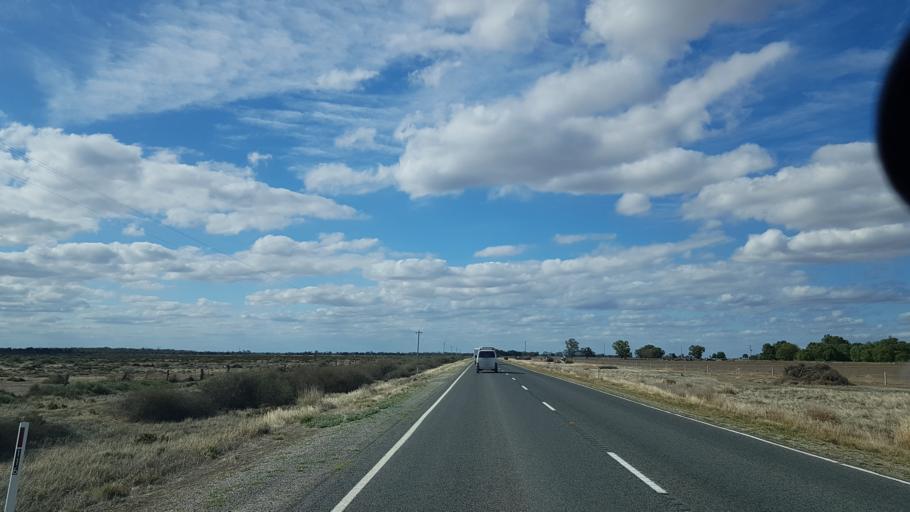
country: AU
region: Victoria
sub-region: Swan Hill
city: Swan Hill
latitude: -35.8389
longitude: 143.9404
